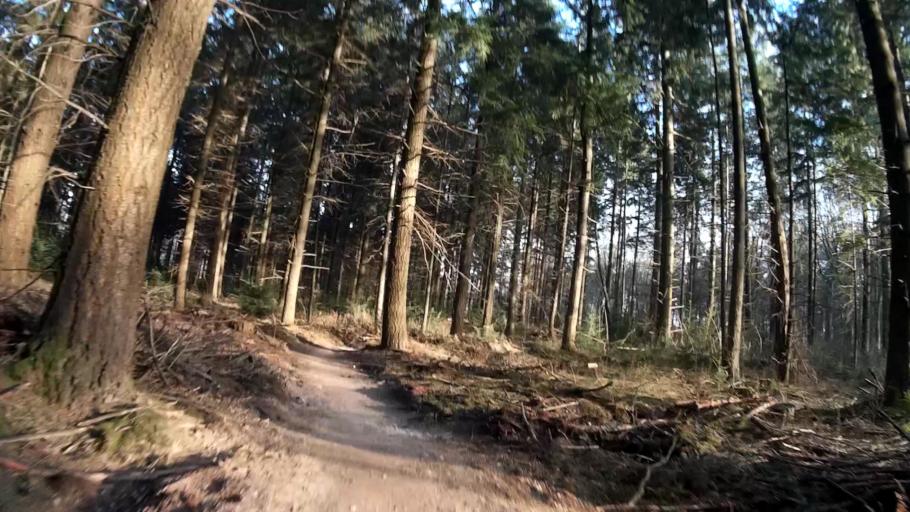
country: NL
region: Utrecht
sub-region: Gemeente Rhenen
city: Rhenen
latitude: 51.9745
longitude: 5.5525
